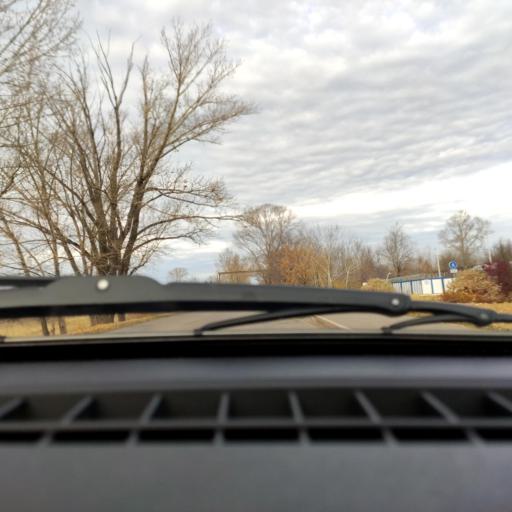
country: RU
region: Bashkortostan
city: Ufa
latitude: 54.8779
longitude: 56.1300
